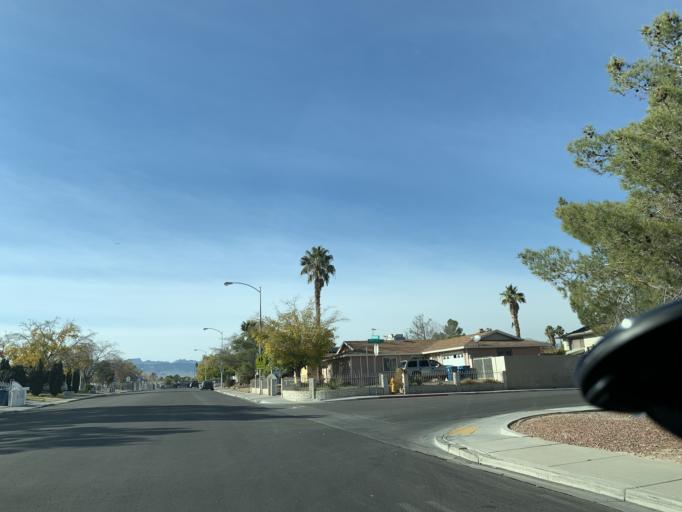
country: US
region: Nevada
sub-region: Clark County
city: Spring Valley
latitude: 36.1090
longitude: -115.2258
